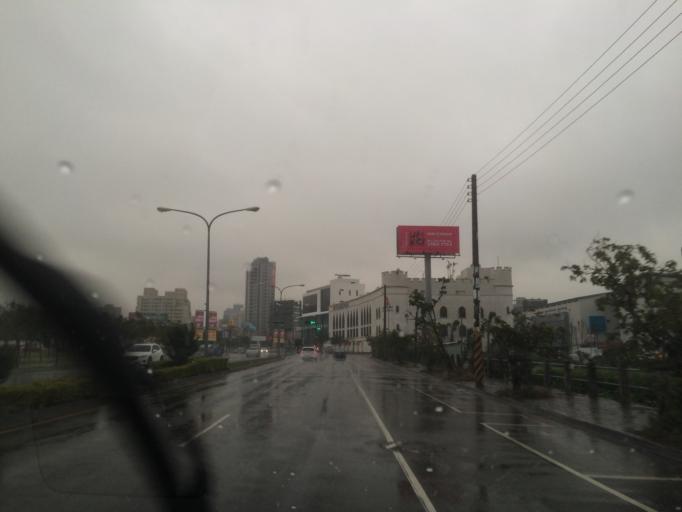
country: TW
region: Taiwan
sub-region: Taichung City
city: Taichung
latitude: 24.1449
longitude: 120.6295
